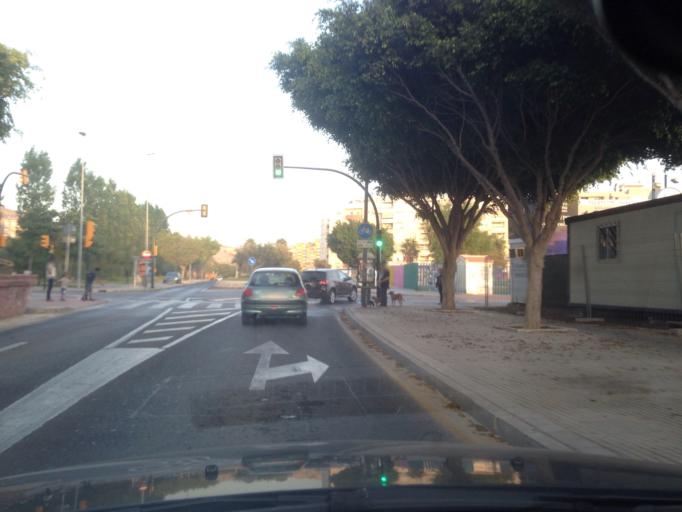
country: ES
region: Andalusia
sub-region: Provincia de Malaga
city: Malaga
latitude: 36.7255
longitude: -4.4637
